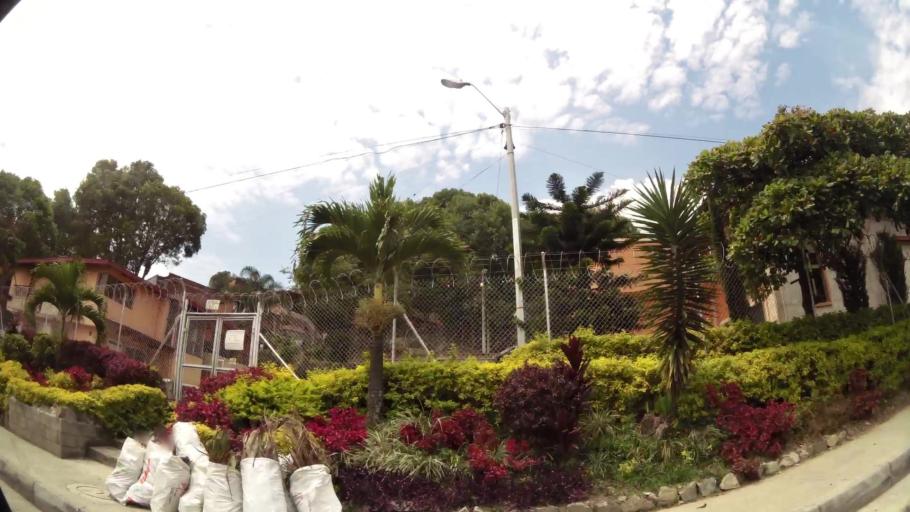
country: CO
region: Antioquia
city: Bello
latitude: 6.3000
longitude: -75.5821
